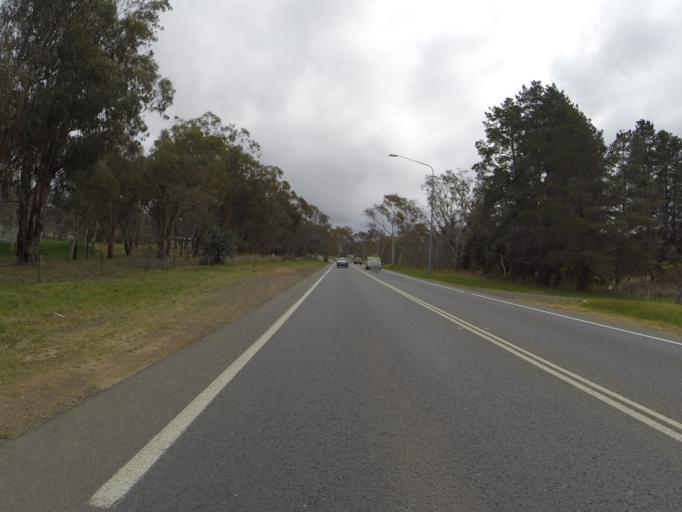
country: AU
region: Australian Capital Territory
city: Canberra
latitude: -35.2894
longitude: 149.1688
